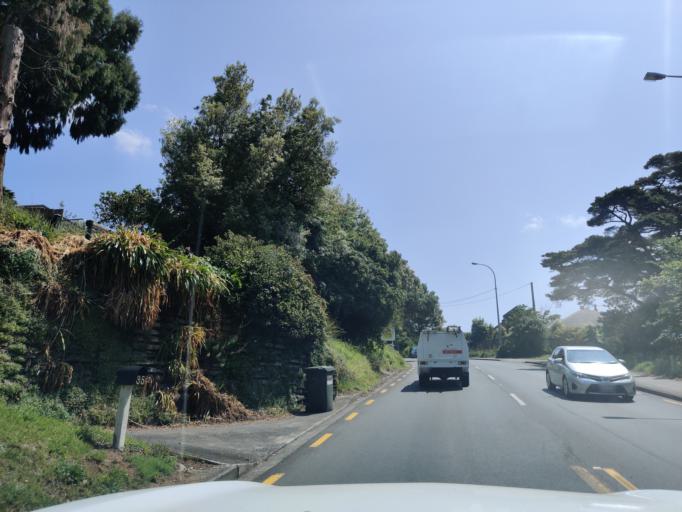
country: NZ
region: Auckland
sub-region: Auckland
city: Pukekohe East
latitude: -37.1985
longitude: 174.9119
